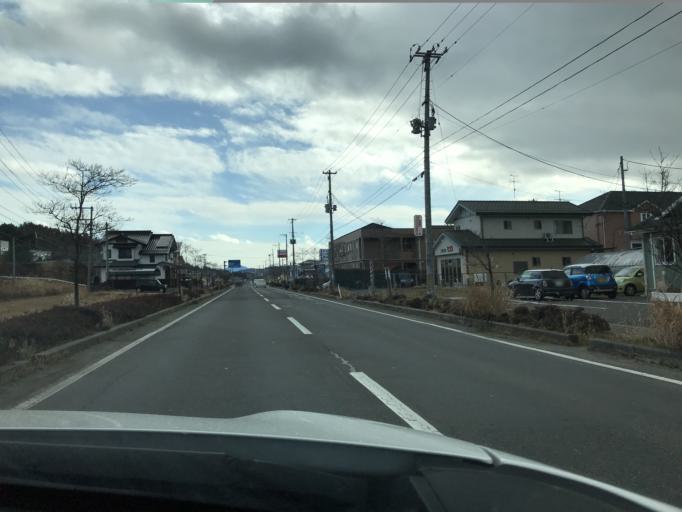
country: JP
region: Fukushima
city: Funehikimachi-funehiki
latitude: 37.4436
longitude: 140.5862
